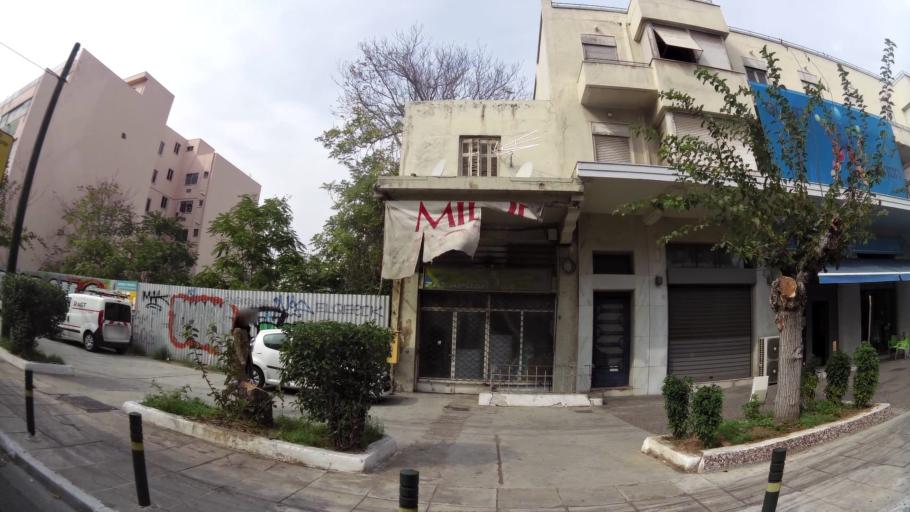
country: GR
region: Attica
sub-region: Nomarchia Athinas
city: Tavros
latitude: 37.9679
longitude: 23.6975
